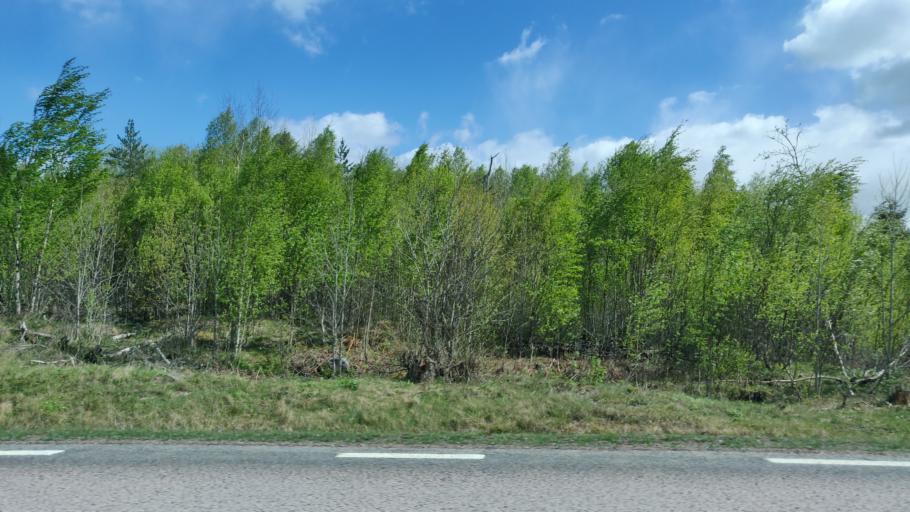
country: SE
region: Vaermland
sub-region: Karlstads Kommun
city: Skattkarr
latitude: 59.5161
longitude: 13.6169
